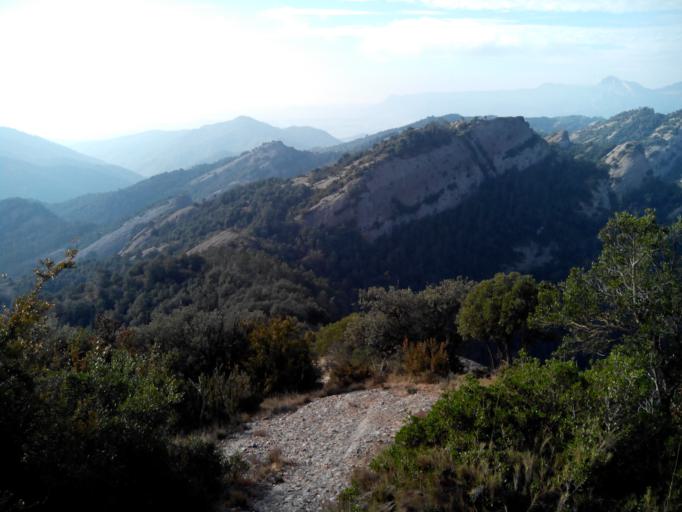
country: ES
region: Catalonia
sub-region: Provincia de Barcelona
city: Vilada
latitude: 42.1183
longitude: 1.9487
